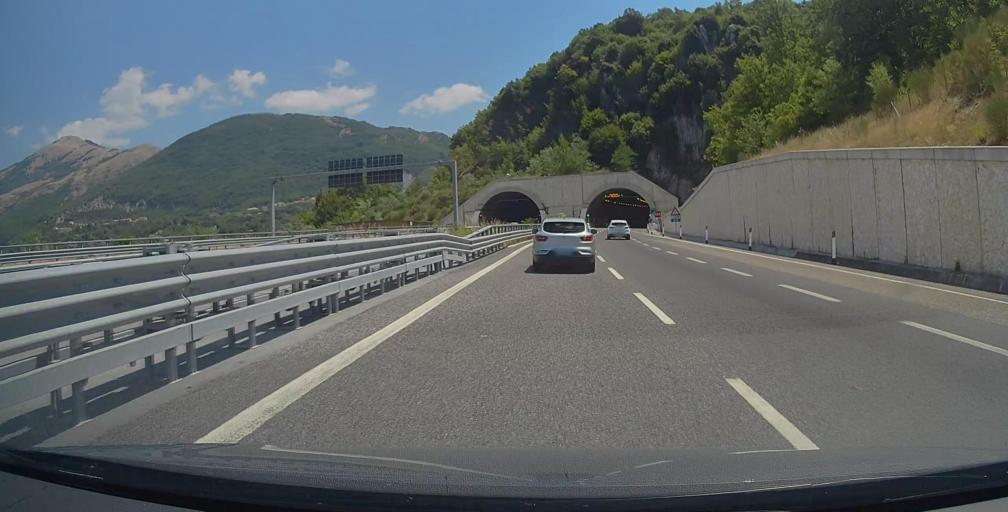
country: IT
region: Calabria
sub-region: Provincia di Cosenza
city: Mormanno
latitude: 39.8995
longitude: 15.9761
